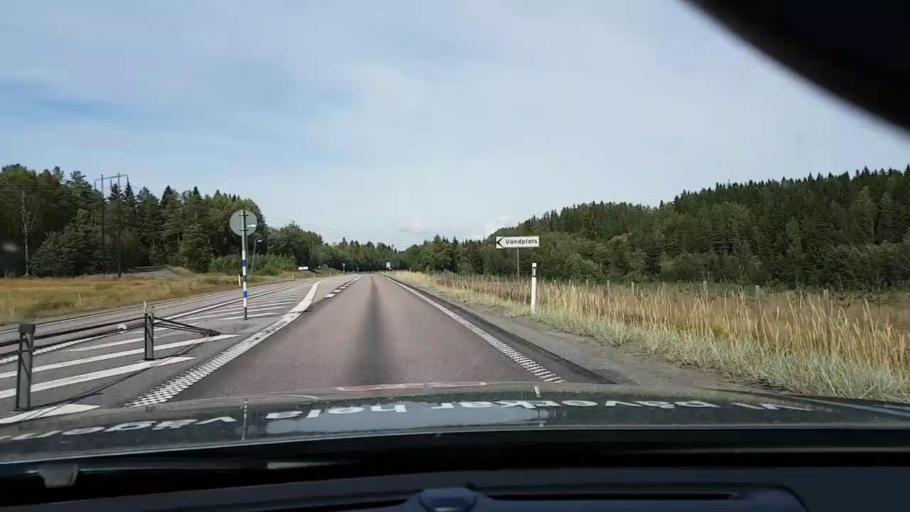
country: SE
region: Vaesternorrland
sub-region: OErnskoeldsviks Kommun
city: Husum
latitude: 63.4181
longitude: 19.2053
